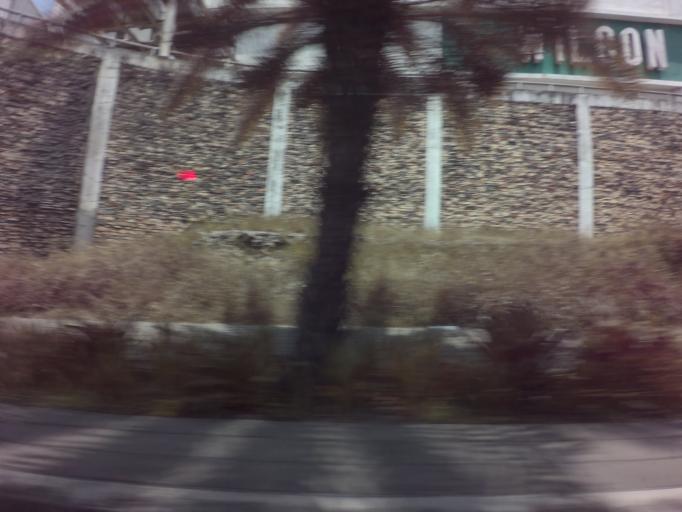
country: PH
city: Sambayanihan People's Village
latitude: 14.4223
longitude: 121.0412
